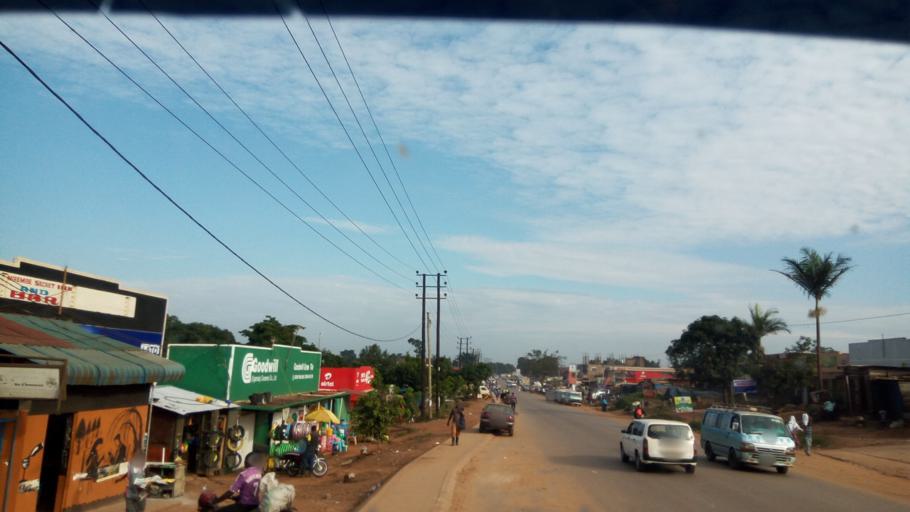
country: UG
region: Central Region
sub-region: Wakiso District
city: Wakiso
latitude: 0.4642
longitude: 32.5230
